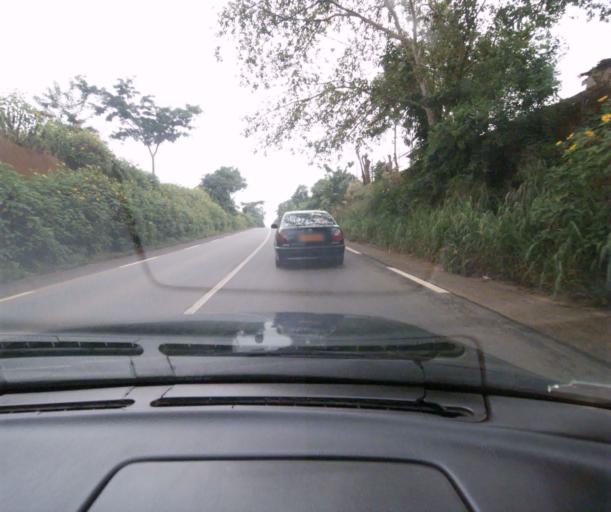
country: CM
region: Centre
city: Obala
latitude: 4.1800
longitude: 11.4712
